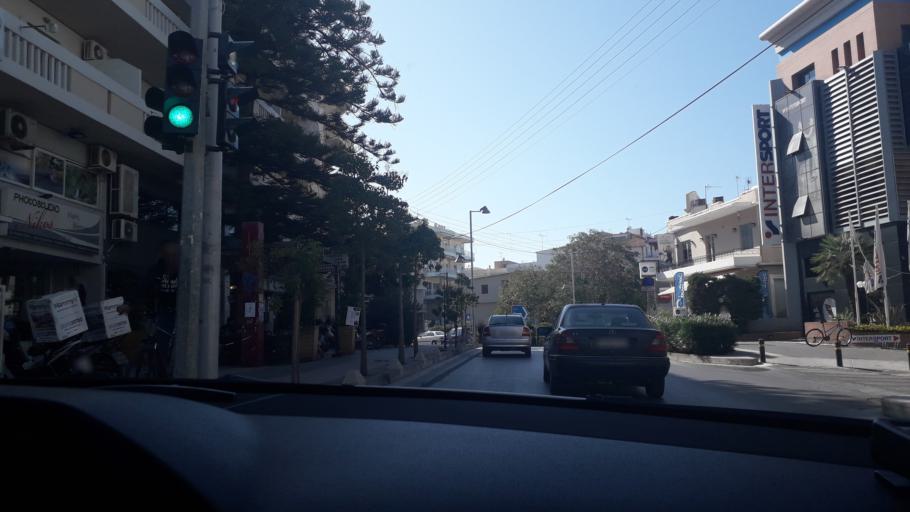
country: GR
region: Crete
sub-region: Nomos Rethymnis
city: Rethymno
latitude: 35.3653
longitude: 24.4811
